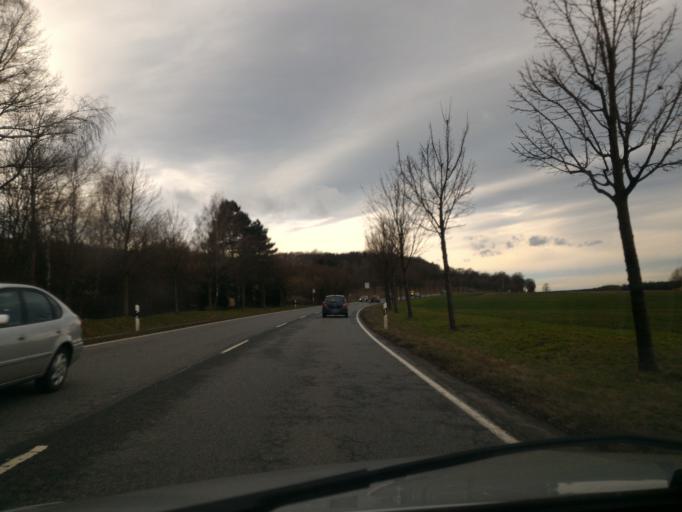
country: DE
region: Saxony
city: Radeberg
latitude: 51.0608
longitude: 13.9202
